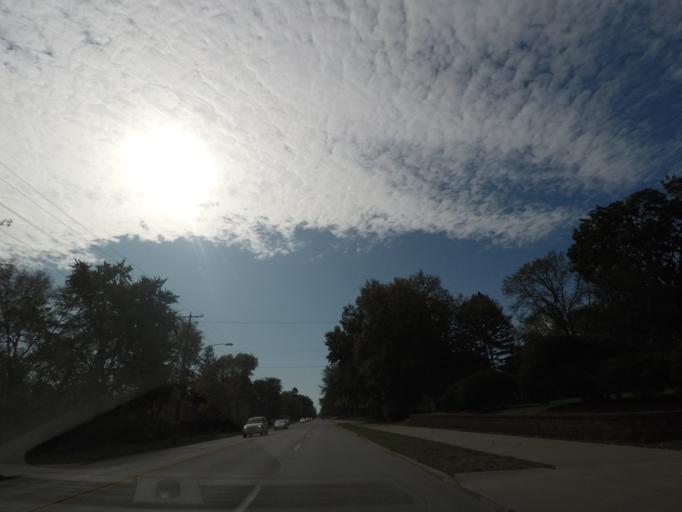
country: US
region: Iowa
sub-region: Story County
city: Ames
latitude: 42.0400
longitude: -93.6205
